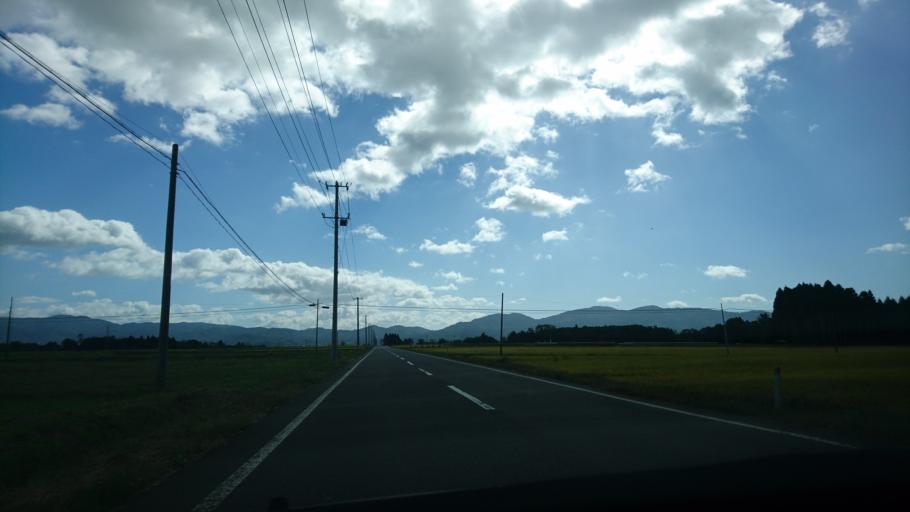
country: JP
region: Iwate
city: Mizusawa
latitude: 39.0746
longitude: 141.1144
